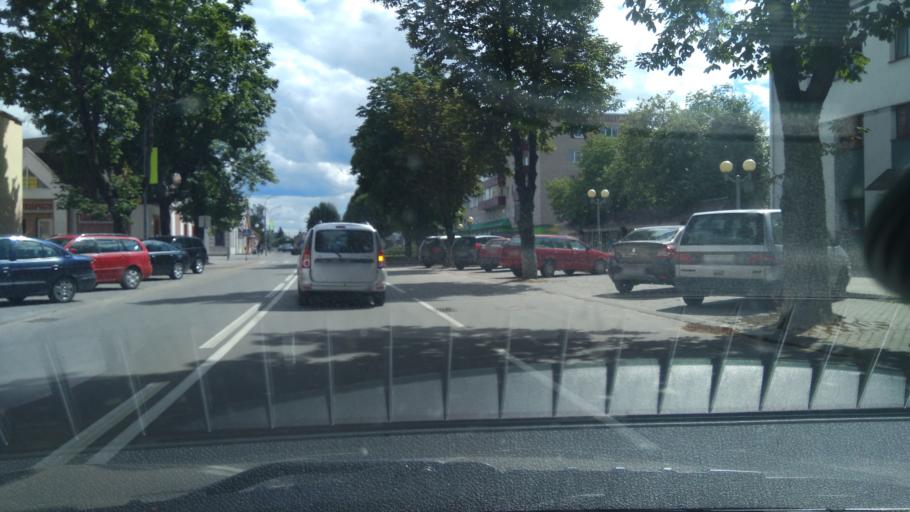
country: BY
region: Grodnenskaya
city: Shchuchin
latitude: 53.6036
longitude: 24.7419
